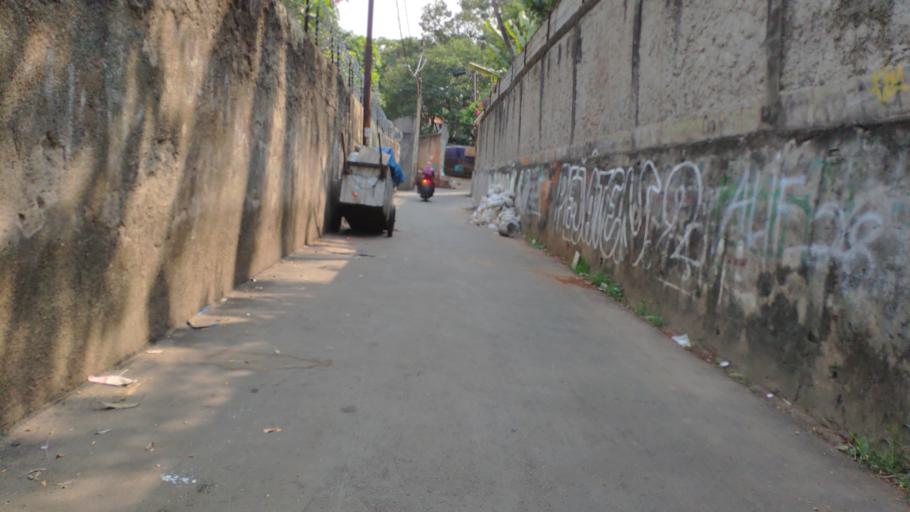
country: ID
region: Jakarta Raya
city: Jakarta
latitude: -6.2738
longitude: 106.8262
